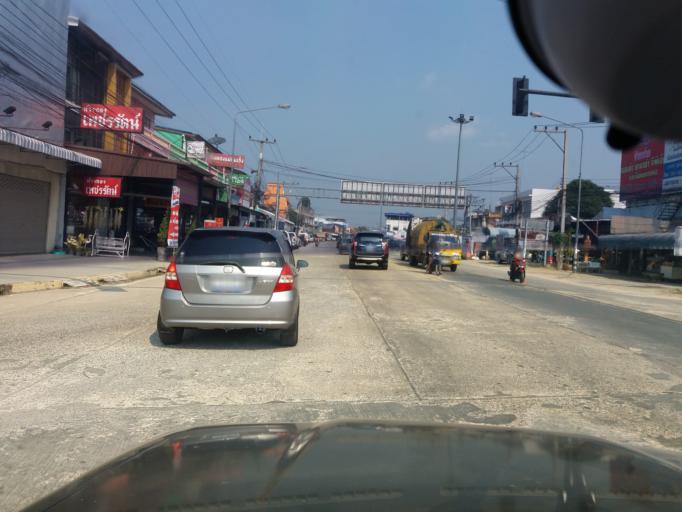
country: TH
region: Sing Buri
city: Bang Racham
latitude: 14.8864
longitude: 100.3138
